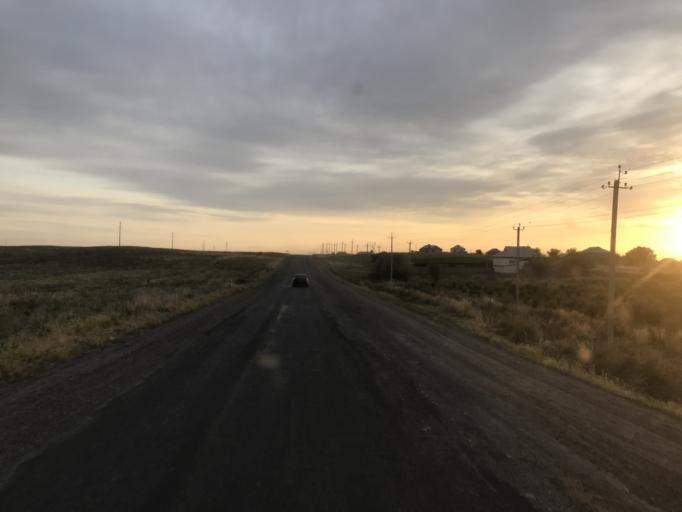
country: UZ
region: Toshkent
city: Amir Timur
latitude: 41.2336
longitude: 68.8103
